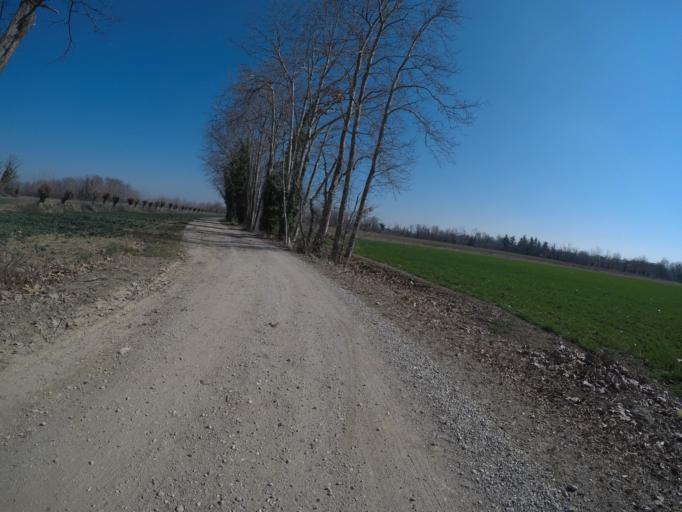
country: IT
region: Friuli Venezia Giulia
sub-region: Provincia di Udine
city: Pozzuolo del Friuli
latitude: 46.0056
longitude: 13.1931
